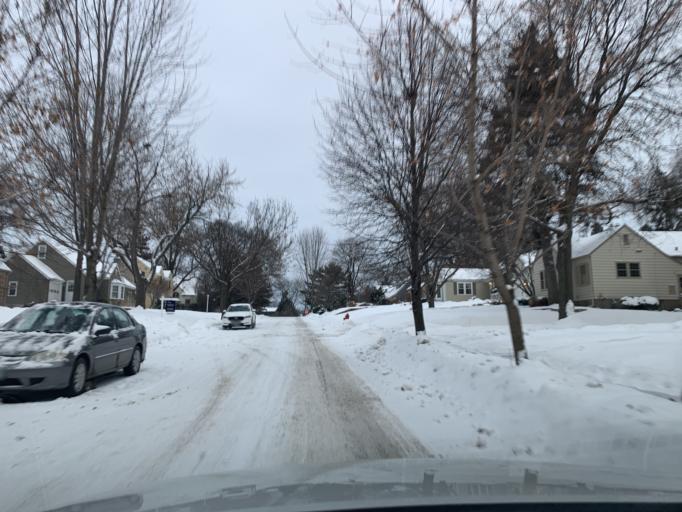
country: US
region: Minnesota
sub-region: Hennepin County
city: Saint Louis Park
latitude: 44.9201
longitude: -93.3472
